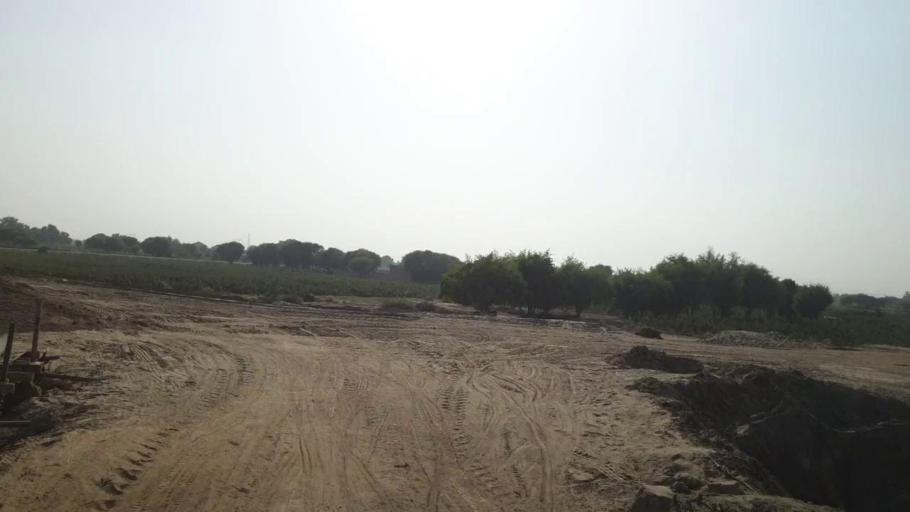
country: PK
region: Sindh
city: Bhan
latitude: 26.5004
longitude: 67.7815
